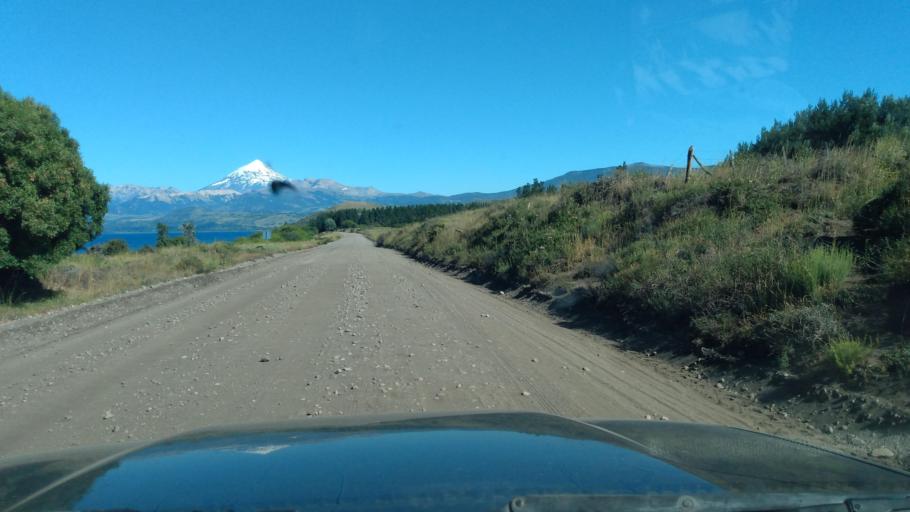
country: AR
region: Neuquen
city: Junin de los Andes
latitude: -39.7894
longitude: -71.2190
